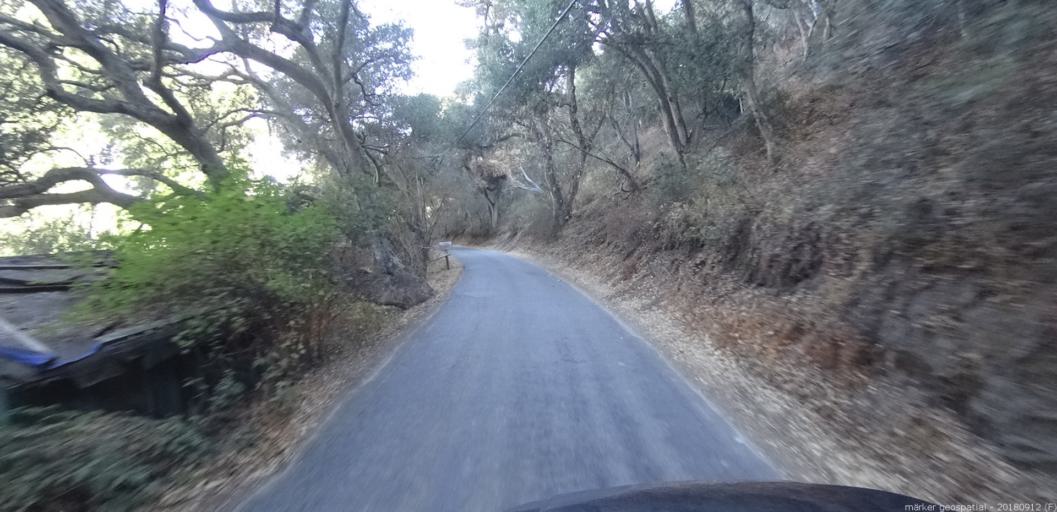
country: US
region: California
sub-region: Monterey County
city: Carmel Valley Village
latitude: 36.5424
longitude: -121.7358
